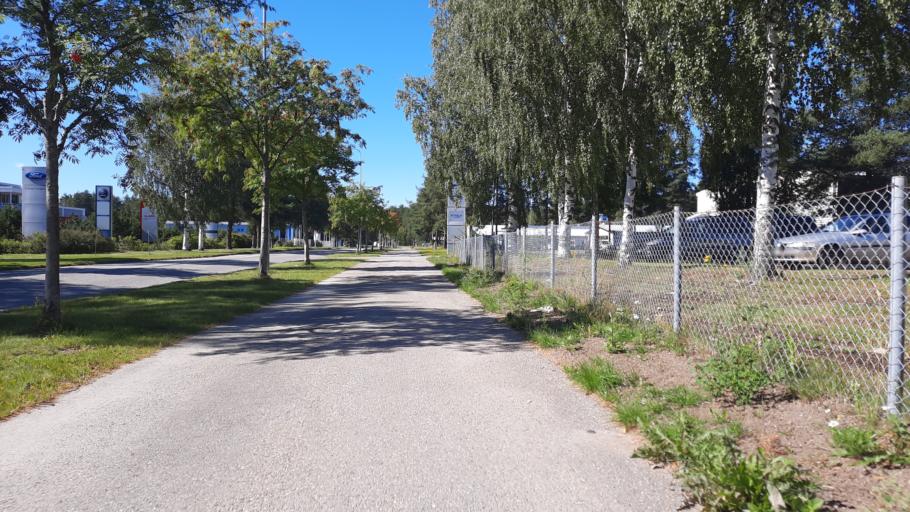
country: FI
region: North Karelia
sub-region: Joensuu
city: Joensuu
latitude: 62.6225
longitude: 29.7426
